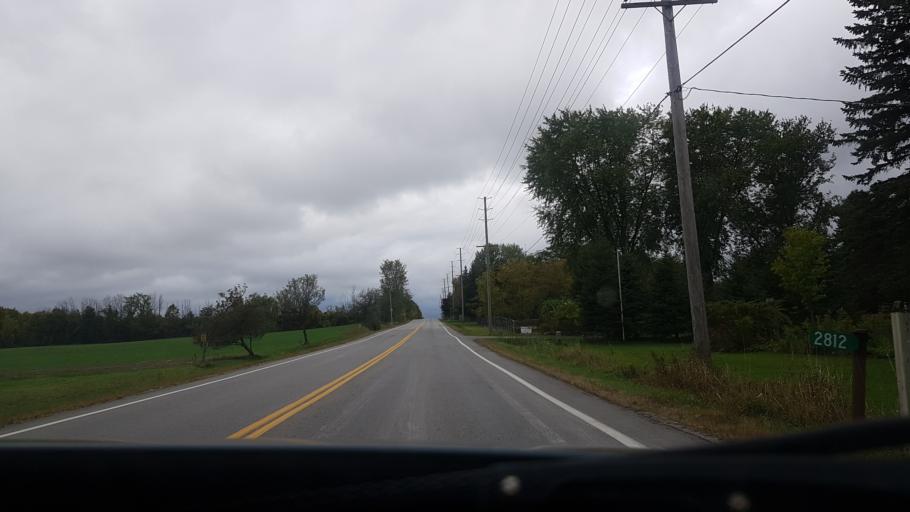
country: CA
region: Ontario
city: Newmarket
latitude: 44.0570
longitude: -79.3851
